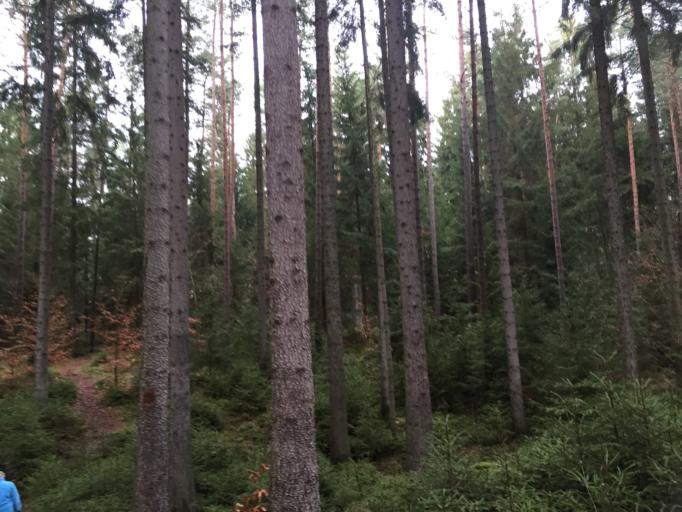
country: DE
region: Thuringia
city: Schleifreisen
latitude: 50.8950
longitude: 11.8114
